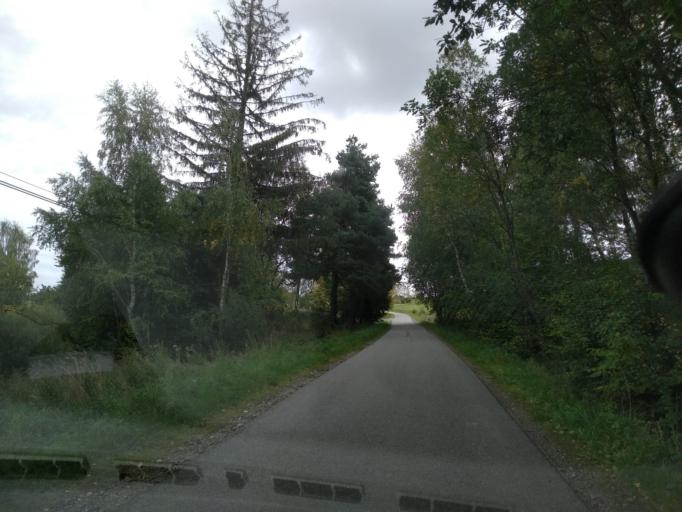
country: PL
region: Lesser Poland Voivodeship
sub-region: Powiat gorlicki
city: Uscie Gorlickie
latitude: 49.5334
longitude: 21.1696
